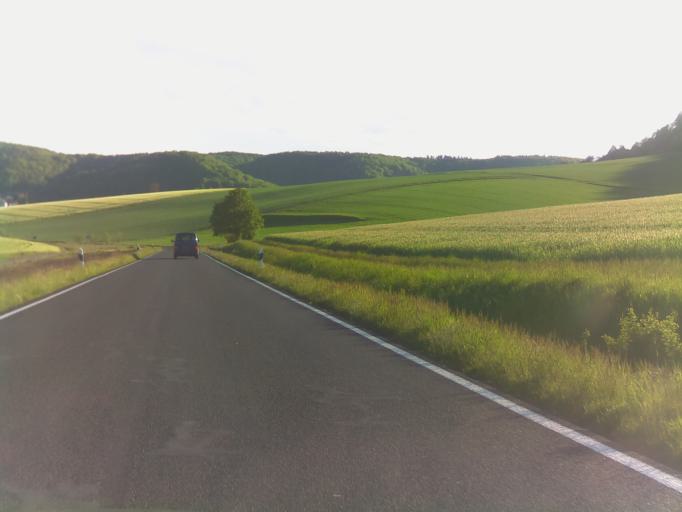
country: DE
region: Bavaria
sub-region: Regierungsbezirk Unterfranken
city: Ramsthal
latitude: 50.1485
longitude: 10.0495
